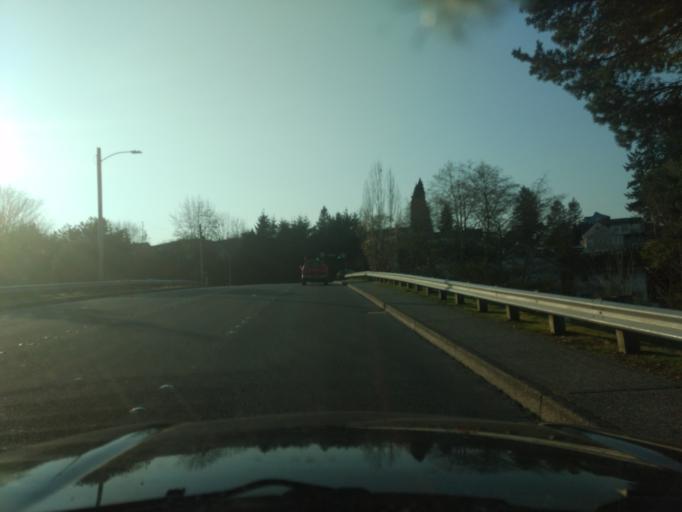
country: US
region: Washington
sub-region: Kitsap County
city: Navy Yard City
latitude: 47.5708
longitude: -122.6554
